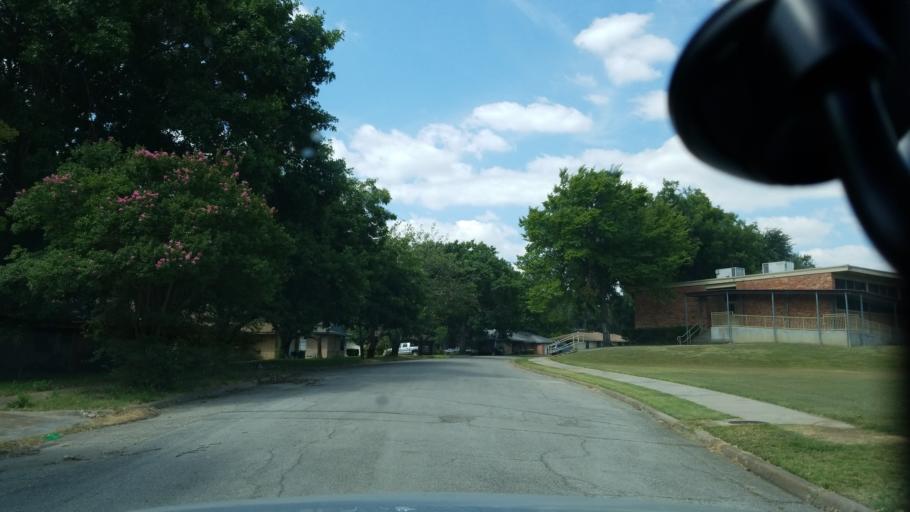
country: US
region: Texas
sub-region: Dallas County
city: Grand Prairie
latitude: 32.7577
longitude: -96.9754
